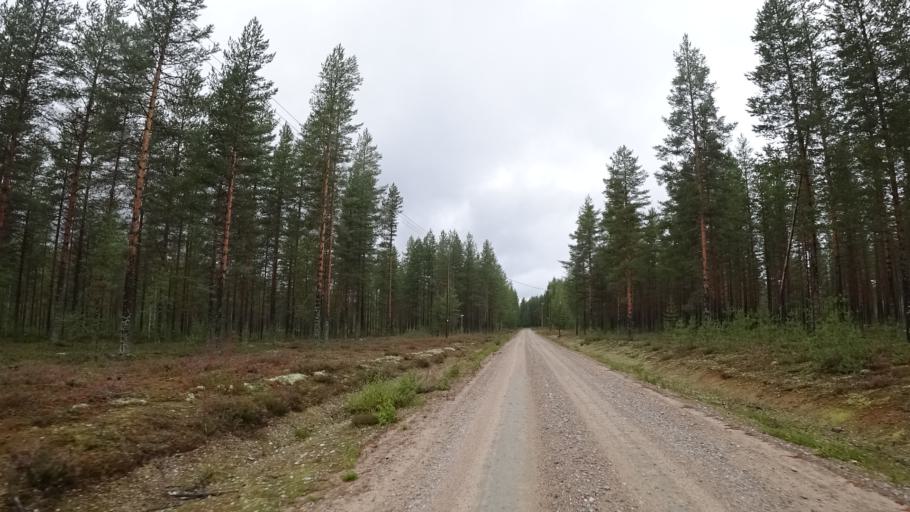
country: FI
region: North Karelia
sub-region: Pielisen Karjala
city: Lieksa
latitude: 63.5376
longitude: 30.0468
